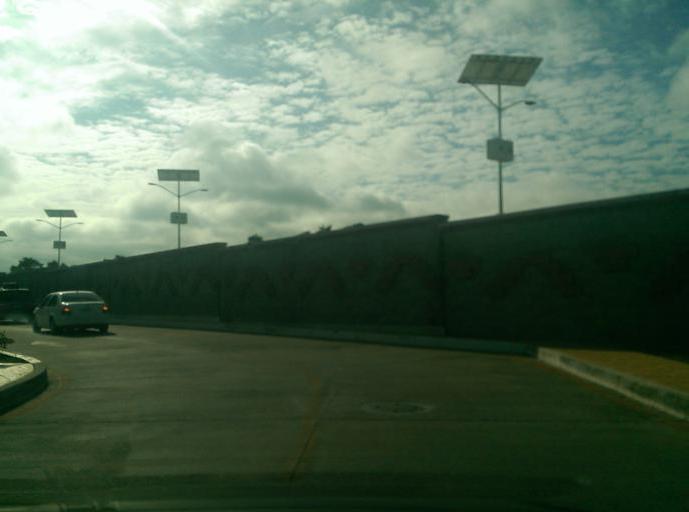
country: MX
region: Chiapas
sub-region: Catazaja
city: Catazaja
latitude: 17.7084
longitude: -92.0193
